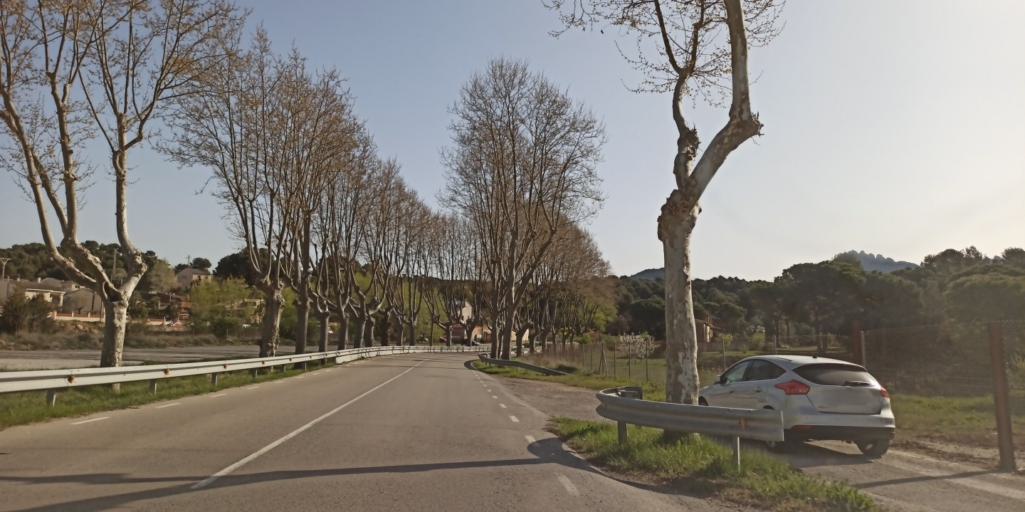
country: ES
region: Catalonia
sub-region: Provincia de Barcelona
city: Castelloli
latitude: 41.6023
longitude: 1.7376
